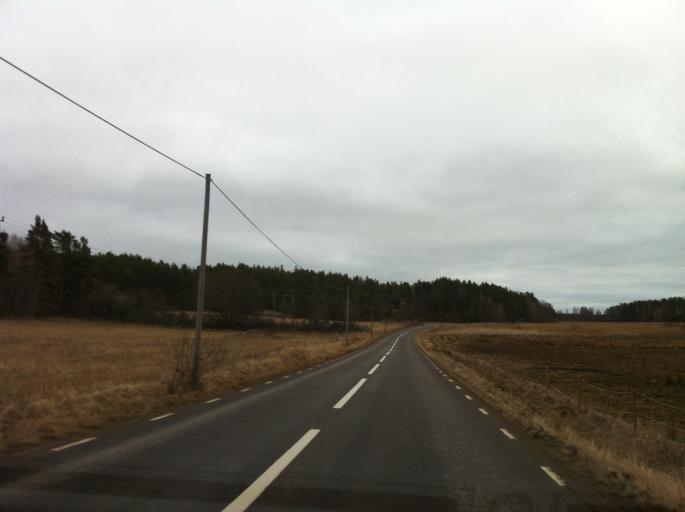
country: SE
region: Kalmar
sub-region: Vasterviks Kommun
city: Overum
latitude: 57.9101
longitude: 16.1770
